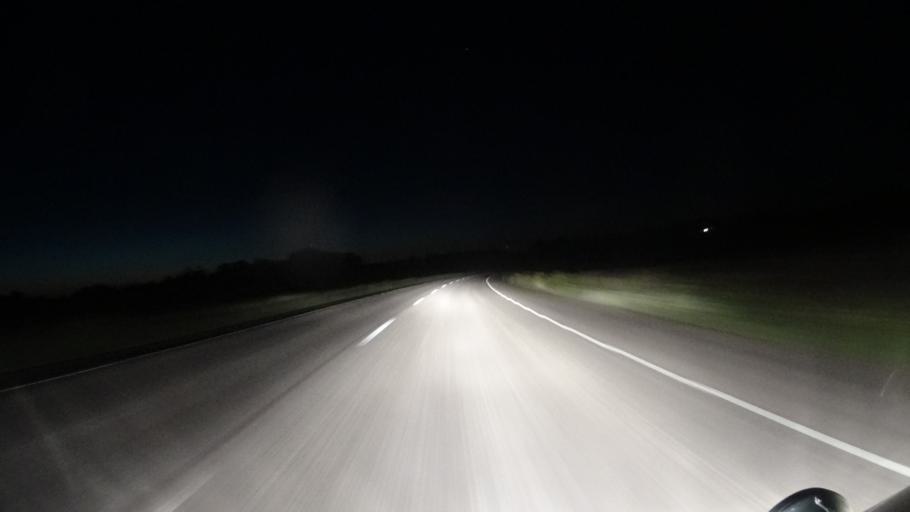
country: SE
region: OEstergoetland
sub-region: Odeshogs Kommun
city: OEdeshoeg
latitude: 58.2510
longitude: 14.7277
